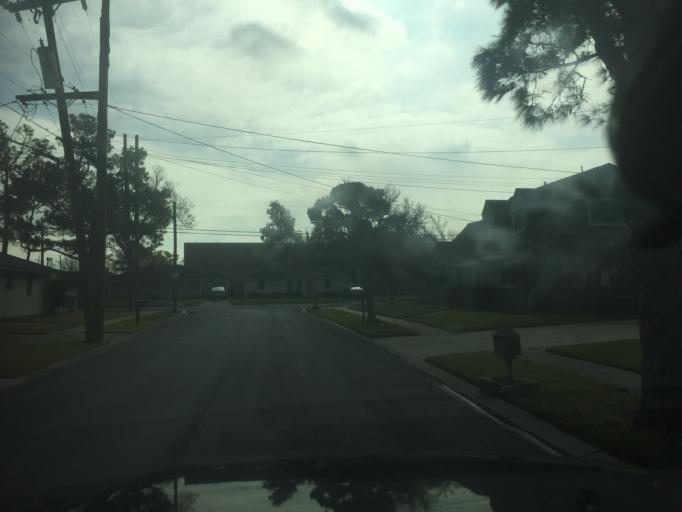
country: US
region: Louisiana
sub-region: Saint Bernard Parish
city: Arabi
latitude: 30.0072
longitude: -90.0382
